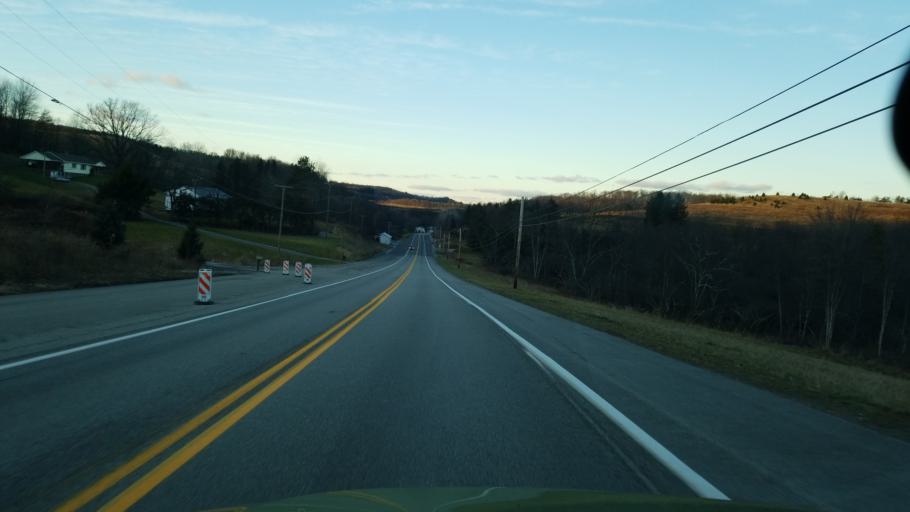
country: US
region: Pennsylvania
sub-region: Indiana County
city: Chevy Chase Heights
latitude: 40.7059
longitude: -79.0997
